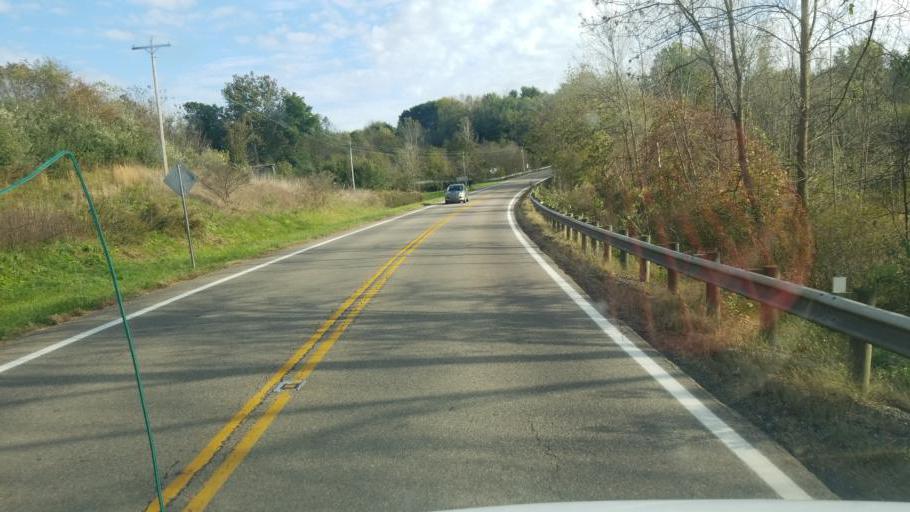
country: US
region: Ohio
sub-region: Wayne County
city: Shreve
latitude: 40.6667
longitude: -81.9456
